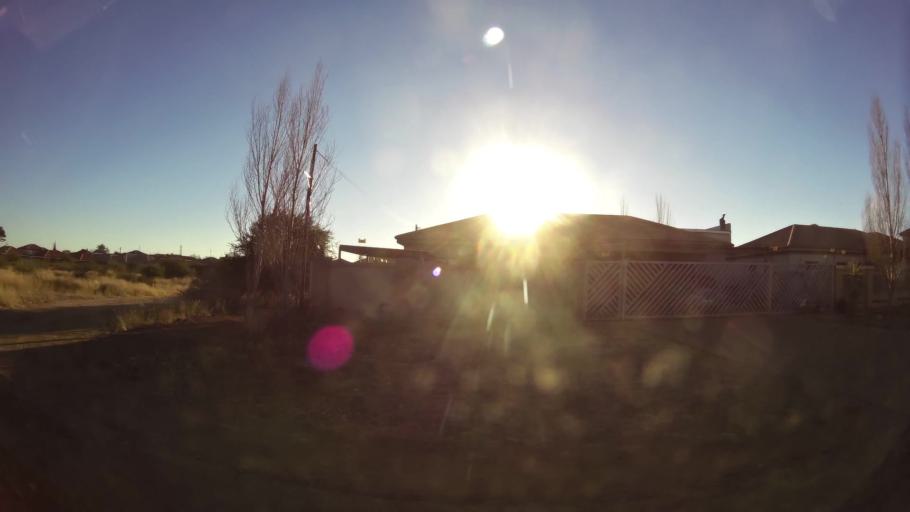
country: ZA
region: Northern Cape
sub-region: Frances Baard District Municipality
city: Kimberley
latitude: -28.7590
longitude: 24.7411
